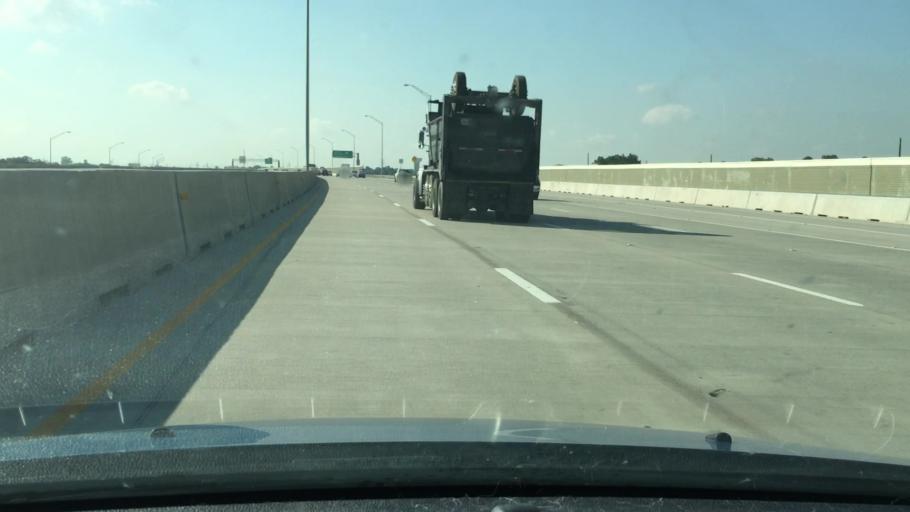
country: US
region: Texas
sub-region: Denton County
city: Highland Village
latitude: 33.0966
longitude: -97.0289
